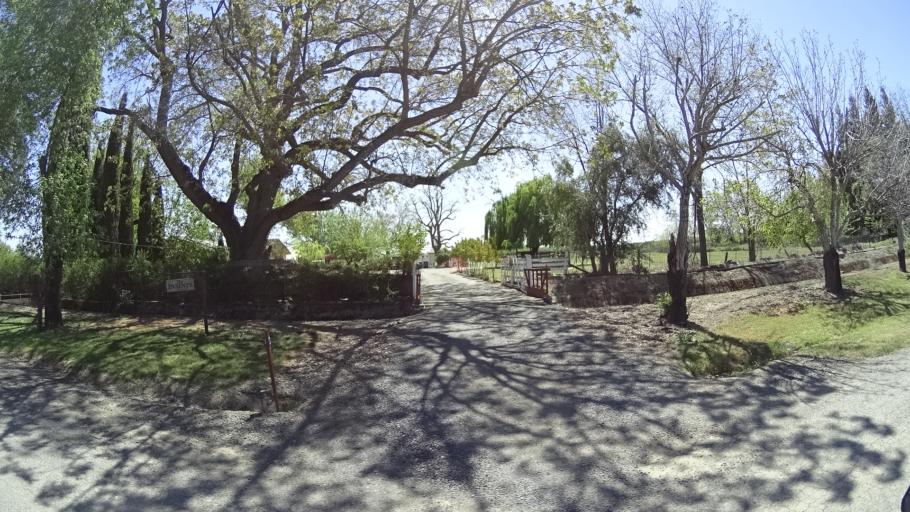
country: US
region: California
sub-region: Glenn County
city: Orland
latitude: 39.7322
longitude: -122.1117
